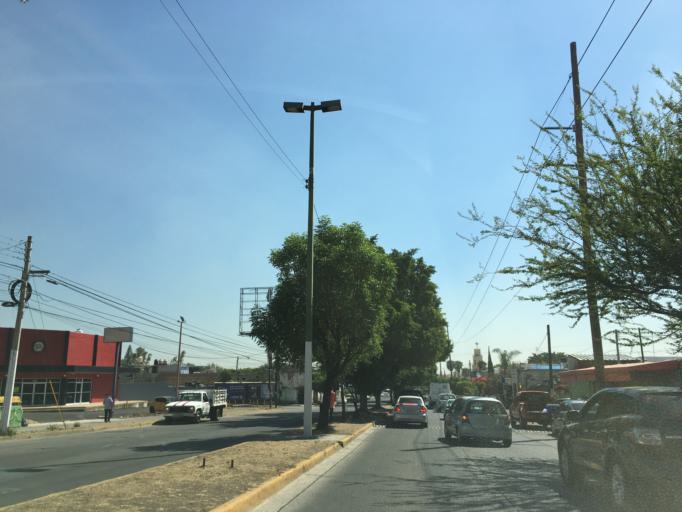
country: MX
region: Jalisco
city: Guadalajara
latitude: 20.6292
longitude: -103.4076
